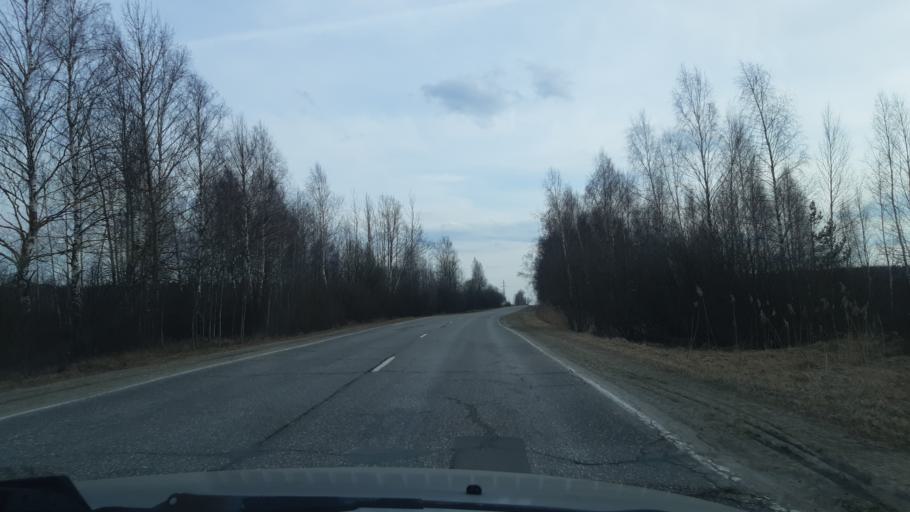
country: RU
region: Vladimir
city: Luknovo
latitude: 56.2085
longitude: 42.0325
